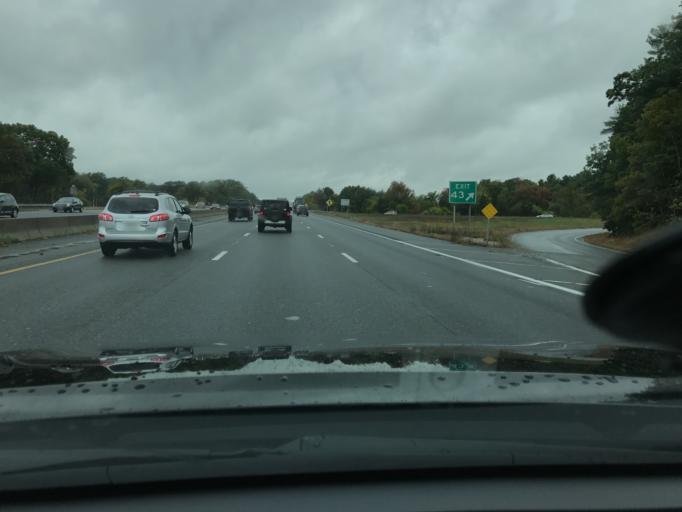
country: US
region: Massachusetts
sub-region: Essex County
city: Lynnfield
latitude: 42.5144
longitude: -71.0245
